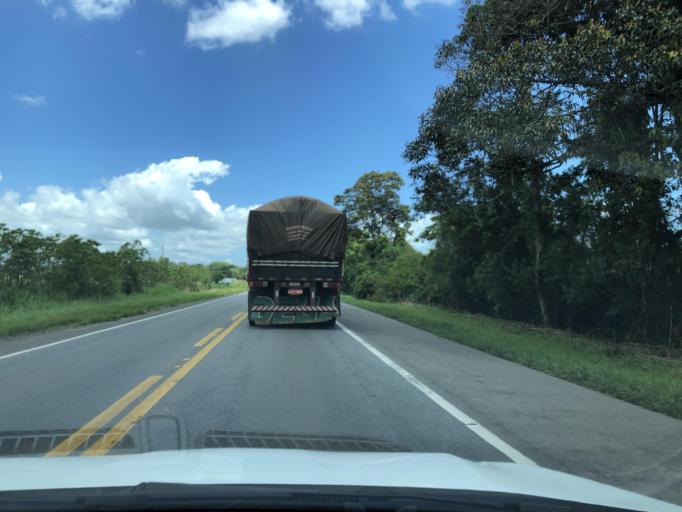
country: BR
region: Santa Catarina
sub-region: Sao Francisco Do Sul
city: Sao Francisco do Sul
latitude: -26.3700
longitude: -48.6839
